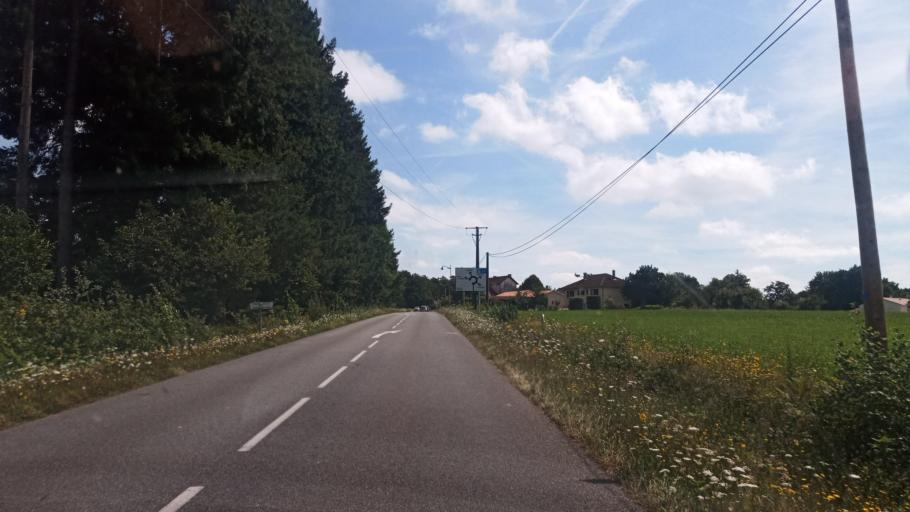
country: FR
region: Limousin
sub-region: Departement de la Haute-Vienne
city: Veyrac
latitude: 45.9011
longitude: 1.0843
